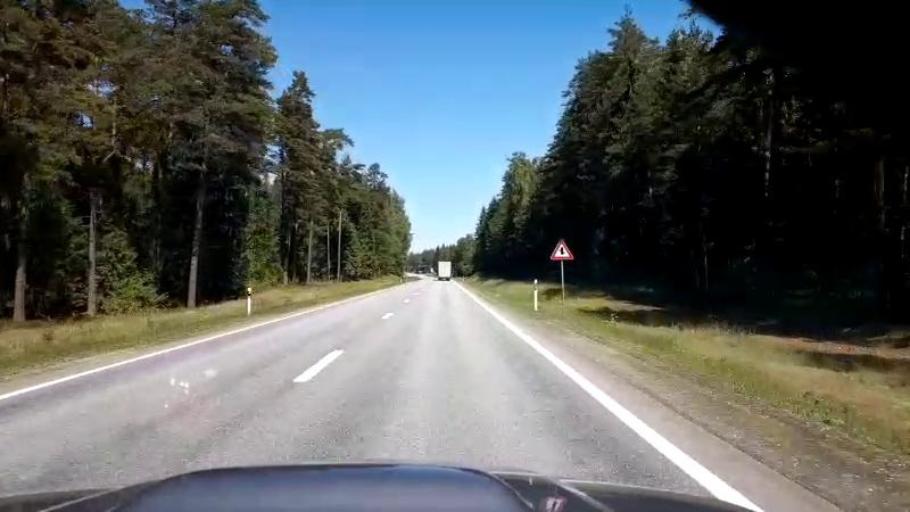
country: LV
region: Salacgrivas
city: Salacgriva
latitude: 57.5685
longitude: 24.4344
